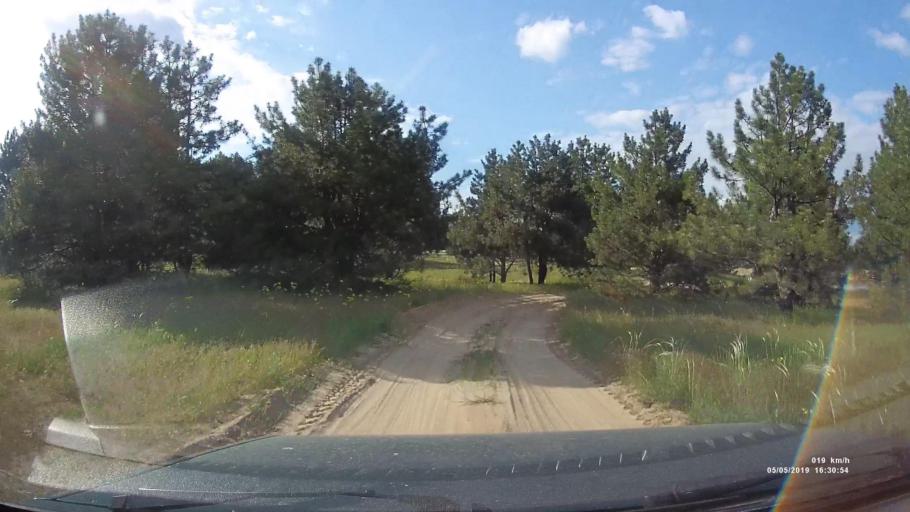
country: RU
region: Rostov
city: Ust'-Donetskiy
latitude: 47.7750
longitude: 41.0154
